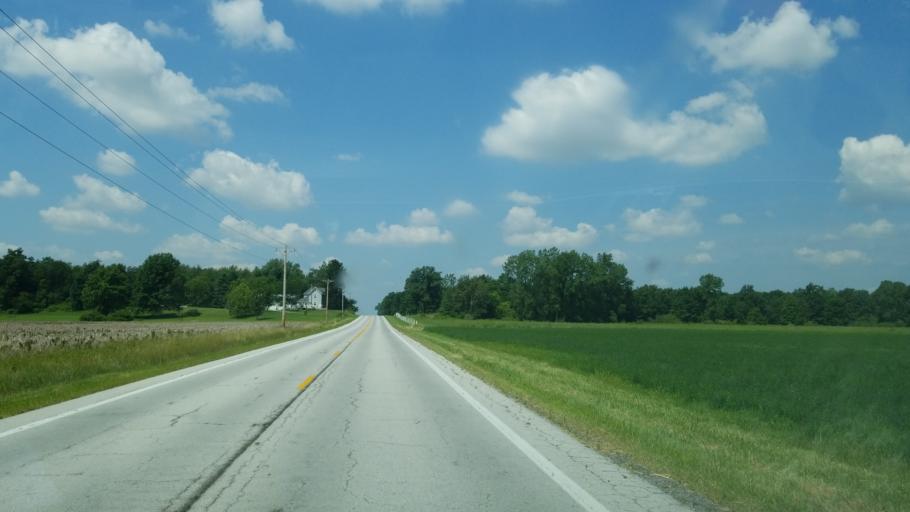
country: US
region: Ohio
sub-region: Wood County
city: Weston
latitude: 41.2842
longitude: -83.7315
